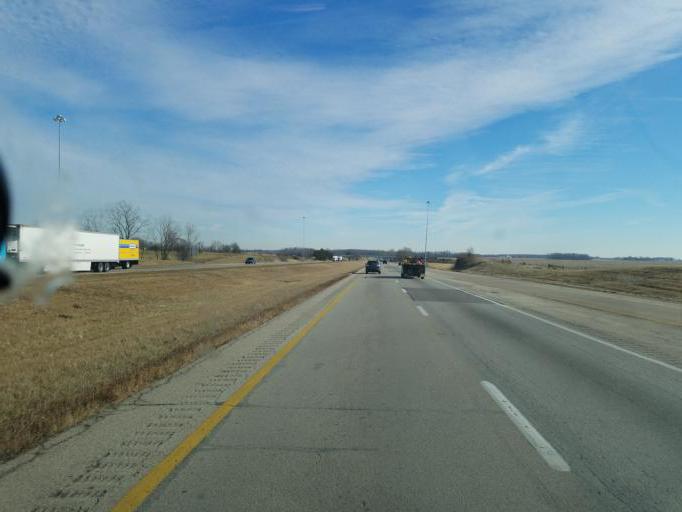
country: US
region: Ohio
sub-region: Preble County
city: New Paris
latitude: 39.8285
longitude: -84.7562
